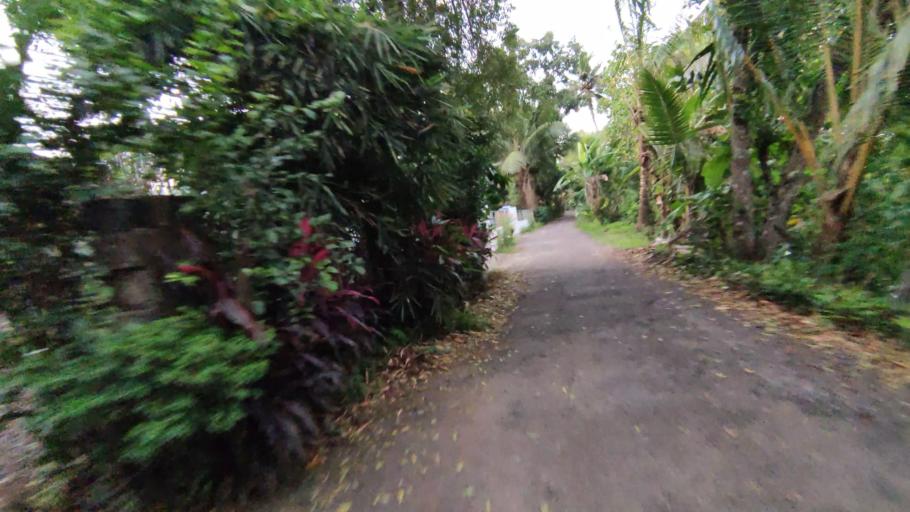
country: IN
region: Kerala
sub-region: Kottayam
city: Kottayam
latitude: 9.5796
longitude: 76.4537
